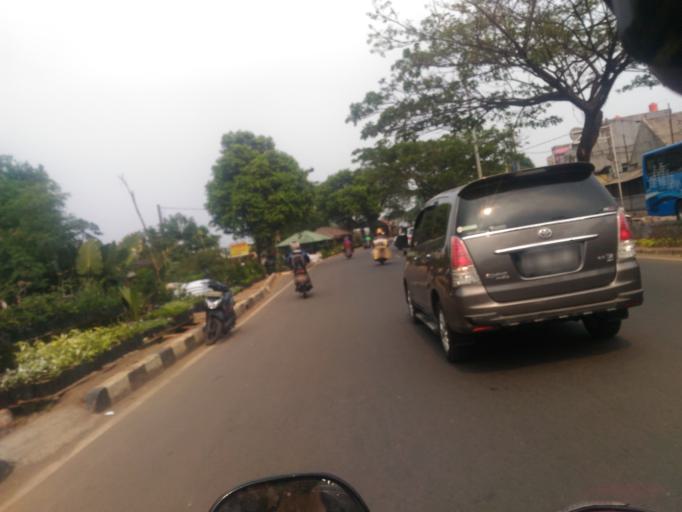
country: ID
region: West Java
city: Depok
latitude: -6.3799
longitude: 106.8531
